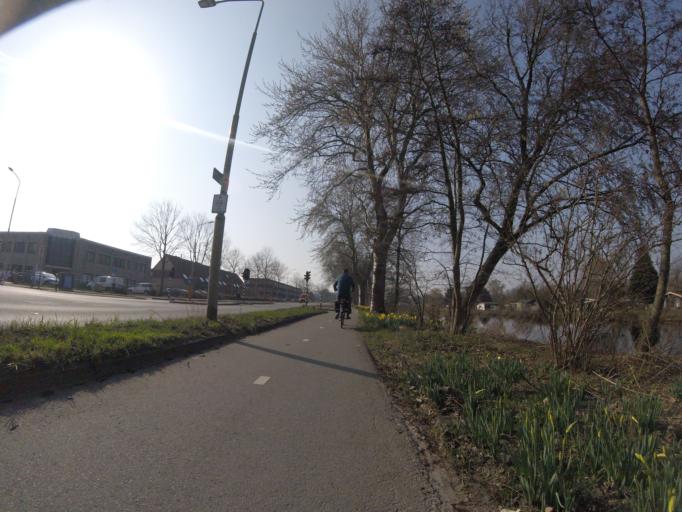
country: NL
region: North Holland
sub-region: Gemeente Haarlem
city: Haarlem
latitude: 52.3679
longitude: 4.6641
